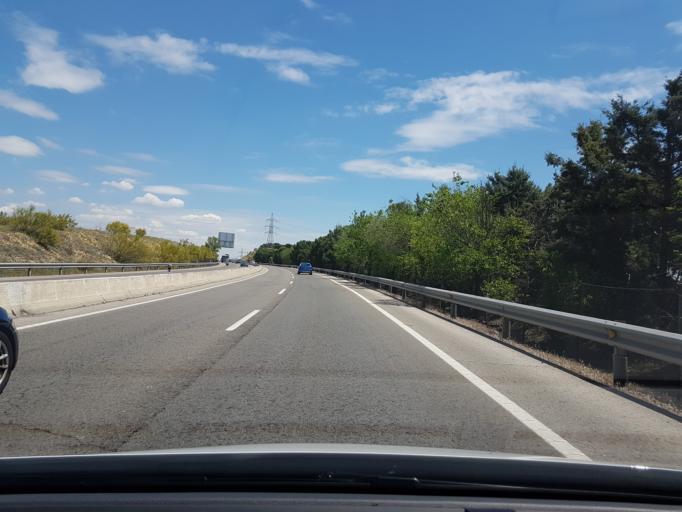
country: ES
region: Madrid
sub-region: Provincia de Madrid
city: Pozuelo de Alarcon
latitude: 40.4415
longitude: -3.7745
